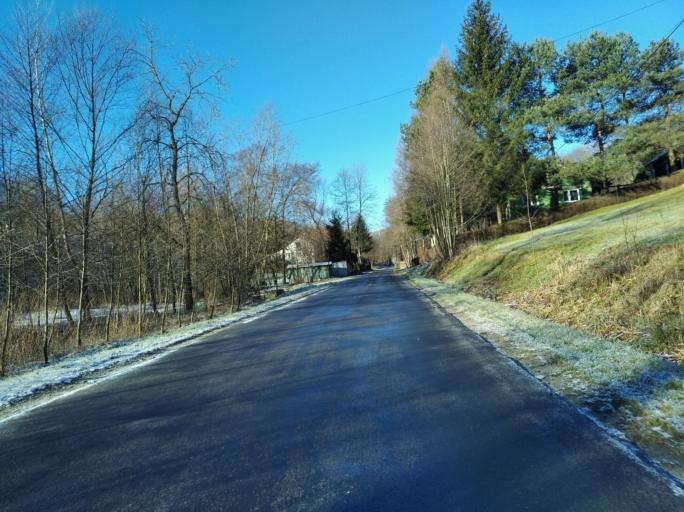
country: PL
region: Subcarpathian Voivodeship
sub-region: Powiat strzyzowski
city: Czudec
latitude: 49.9515
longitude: 21.7755
